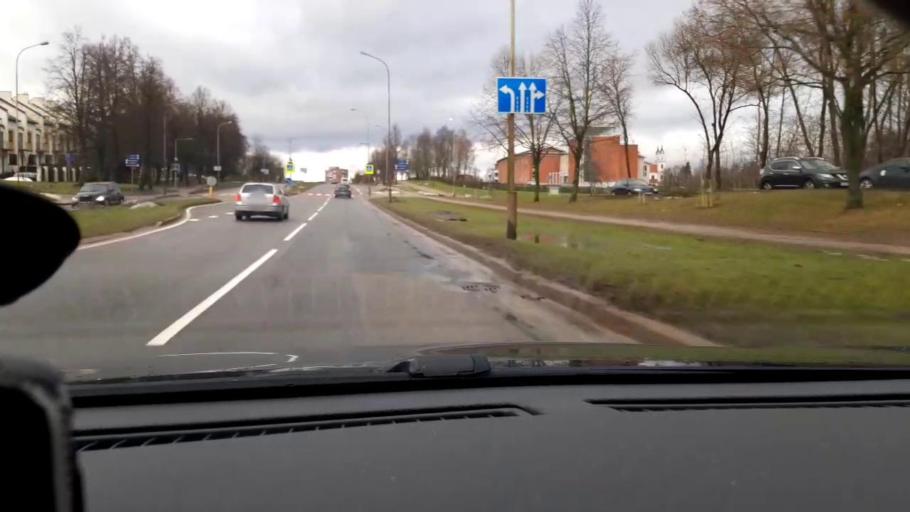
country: LT
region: Vilnius County
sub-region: Vilnius
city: Fabijoniskes
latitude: 54.7356
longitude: 25.2784
